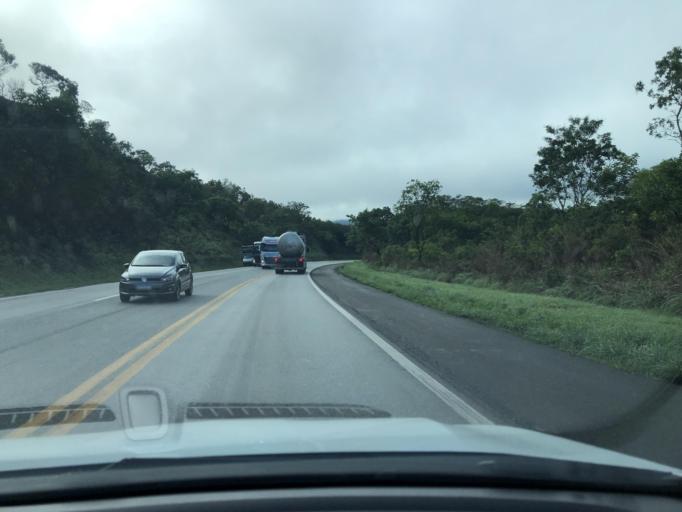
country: BR
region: Goias
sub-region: Luziania
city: Luziania
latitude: -16.3809
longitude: -47.8276
